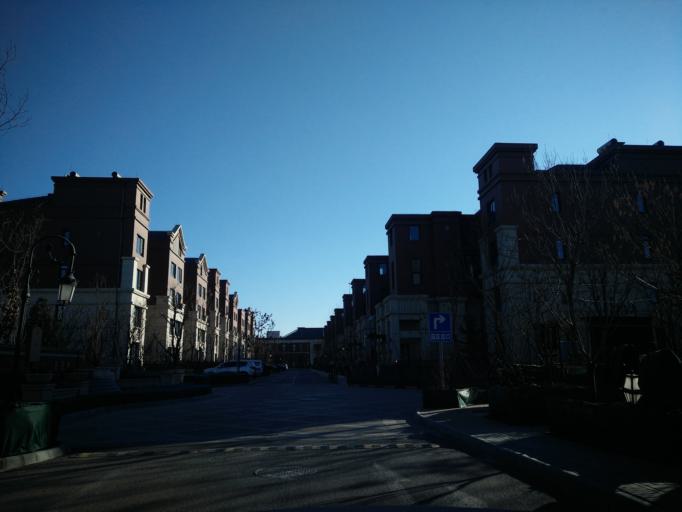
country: CN
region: Beijing
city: Xingfeng
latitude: 39.7060
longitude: 116.3954
